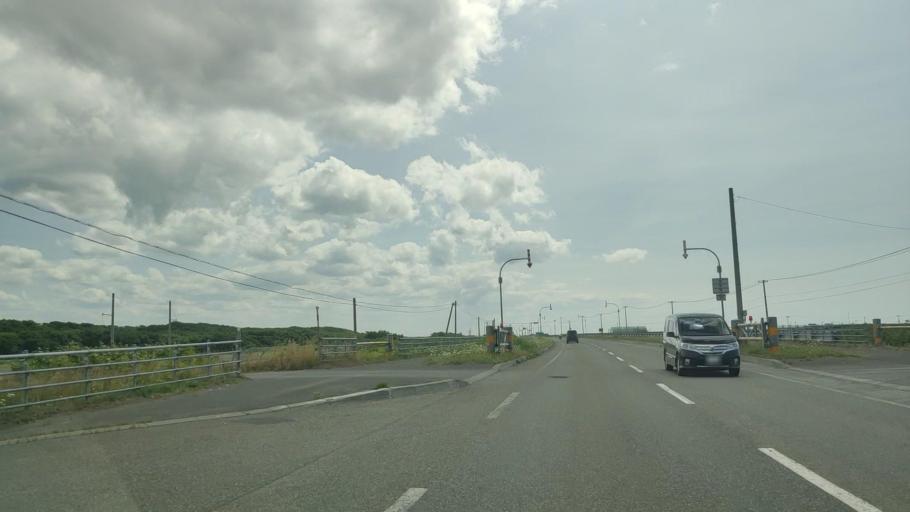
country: JP
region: Hokkaido
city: Makubetsu
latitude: 44.8705
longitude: 141.7521
